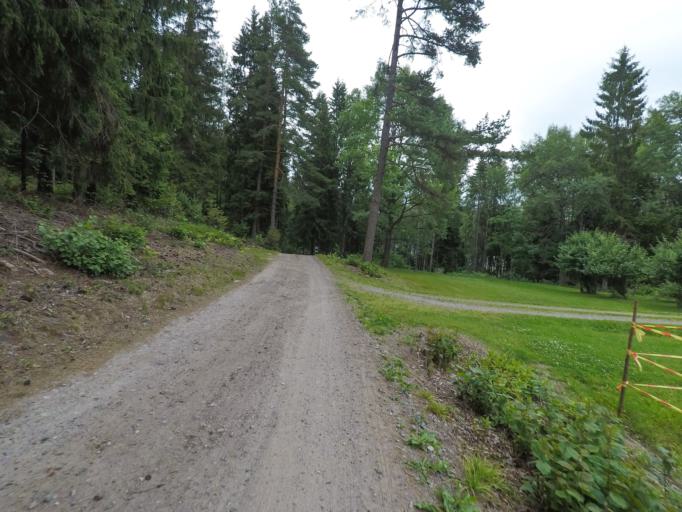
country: FI
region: Uusimaa
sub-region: Helsinki
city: Karjalohja
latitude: 60.2395
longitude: 23.6681
